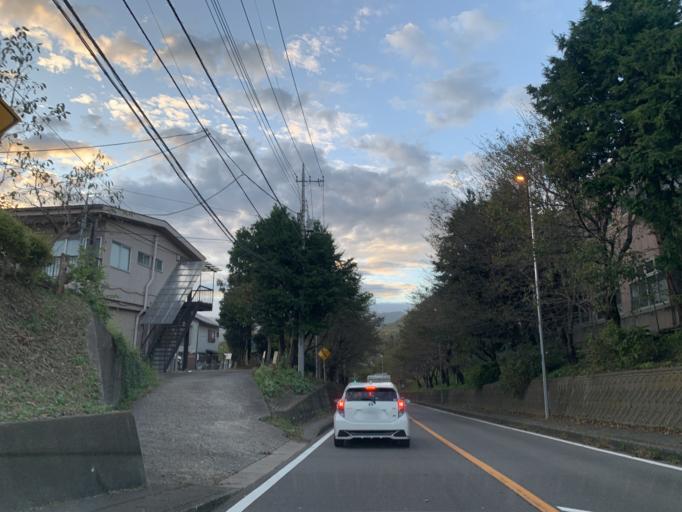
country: JP
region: Yamanashi
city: Otsuki
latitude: 35.6094
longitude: 138.9986
